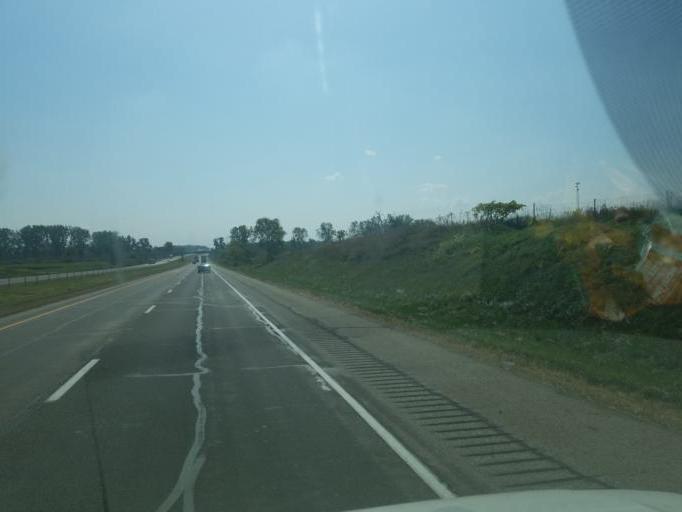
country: US
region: Indiana
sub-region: Steuben County
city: Angola
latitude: 41.5455
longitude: -85.0565
